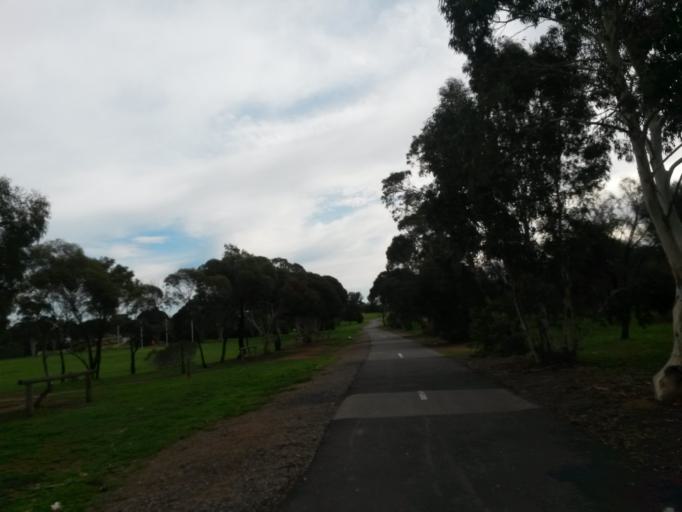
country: AU
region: South Australia
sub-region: Onkaparinga
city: Moana
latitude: -35.1990
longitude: 138.4890
